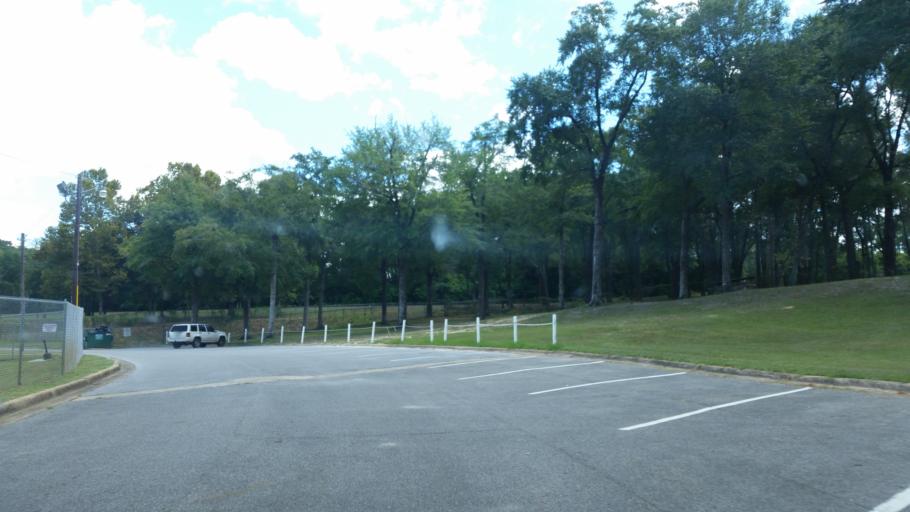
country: US
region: Florida
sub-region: Okaloosa County
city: Crestview
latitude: 30.7606
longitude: -86.5673
